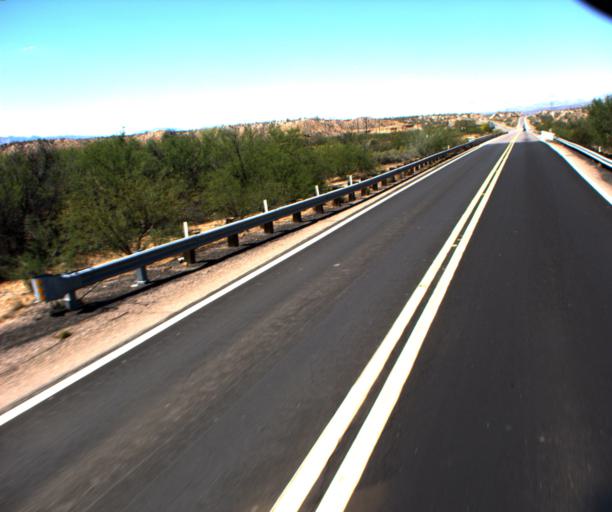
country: US
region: Arizona
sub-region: Yavapai County
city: Bagdad
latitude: 34.7355
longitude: -113.6153
